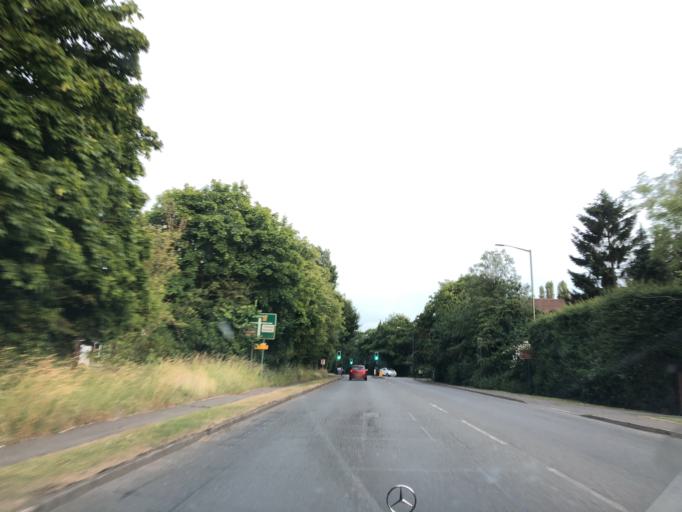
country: GB
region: England
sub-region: Solihull
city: Balsall Common
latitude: 52.3849
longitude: -1.6453
